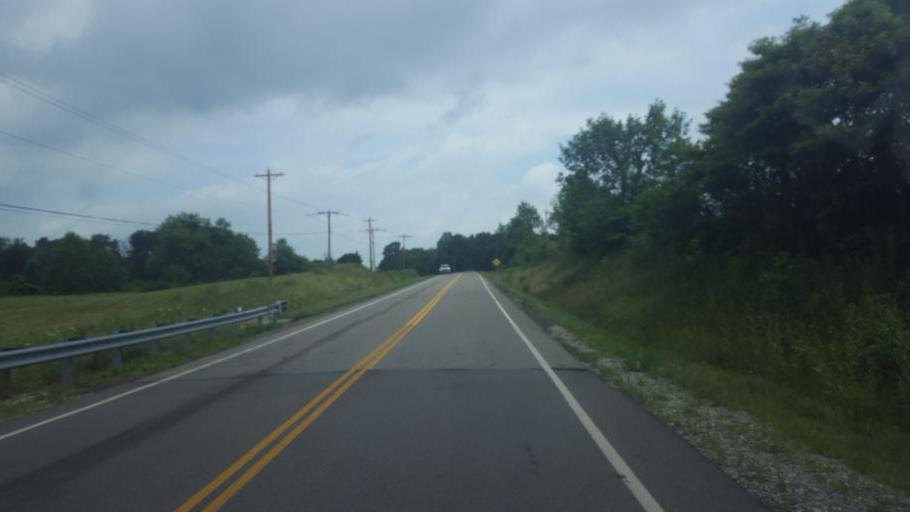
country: US
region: Ohio
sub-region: Licking County
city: Utica
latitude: 40.1807
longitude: -82.5187
